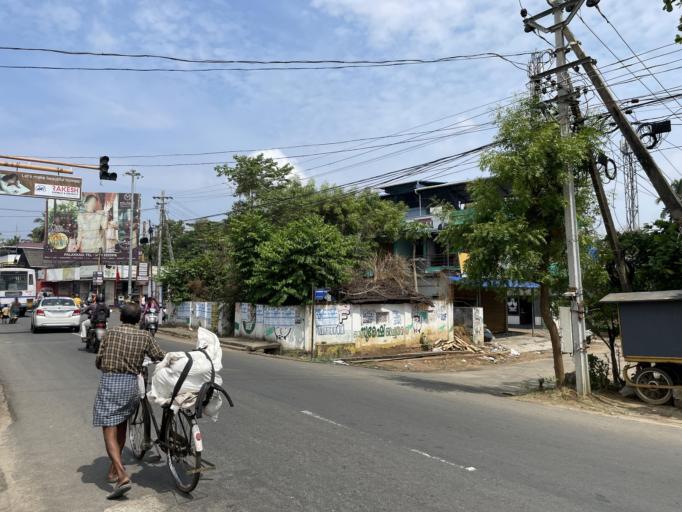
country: IN
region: Kerala
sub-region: Palakkad district
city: Chittur
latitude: 10.6825
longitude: 76.7010
